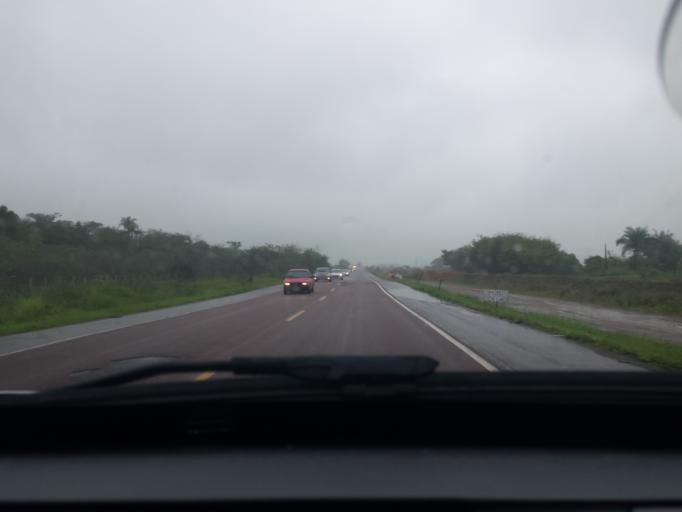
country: BR
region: Santa Catarina
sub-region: Itajai
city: Itajai
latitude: -26.8455
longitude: -48.7974
